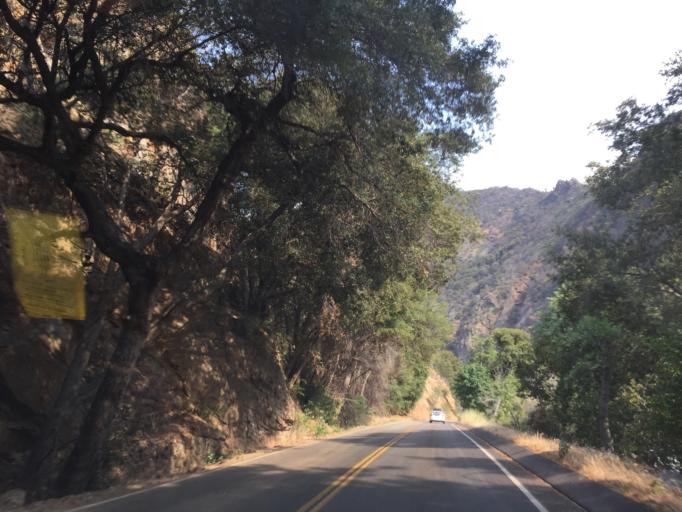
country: US
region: California
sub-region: Tulare County
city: Three Rivers
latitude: 36.8115
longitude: -118.8026
